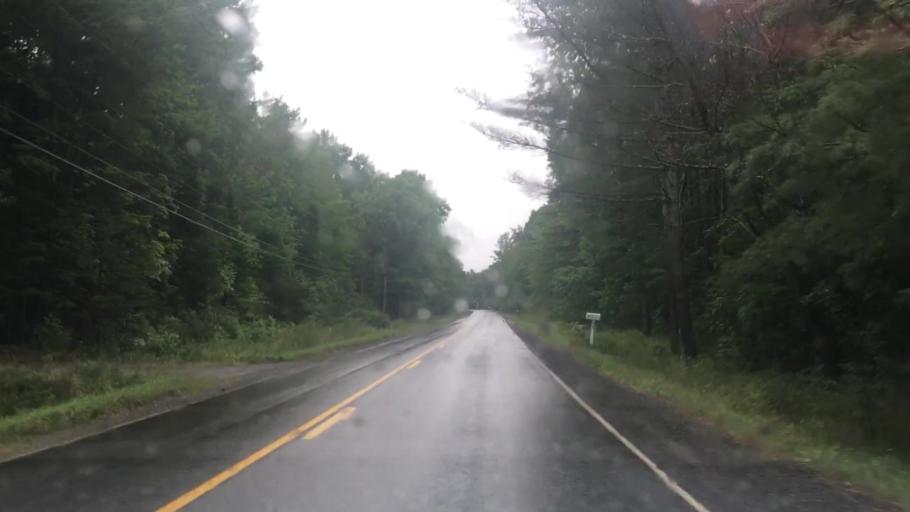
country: US
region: Maine
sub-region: Penobscot County
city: Milford
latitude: 44.9749
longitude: -68.7326
